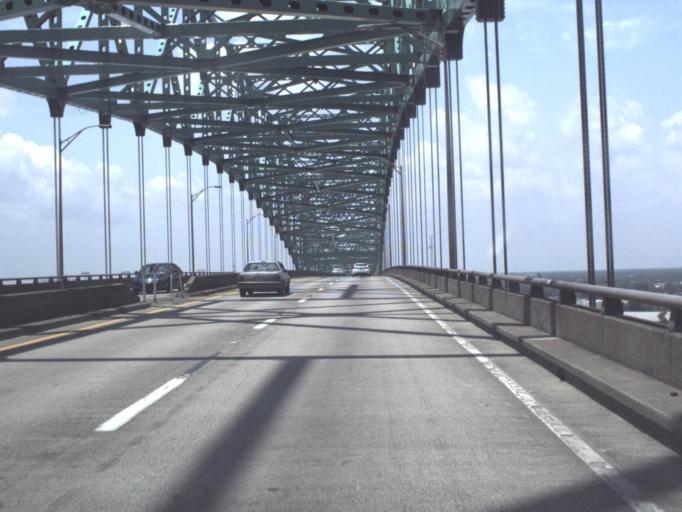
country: US
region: Florida
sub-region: Duval County
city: Jacksonville
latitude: 30.3147
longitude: -81.6268
